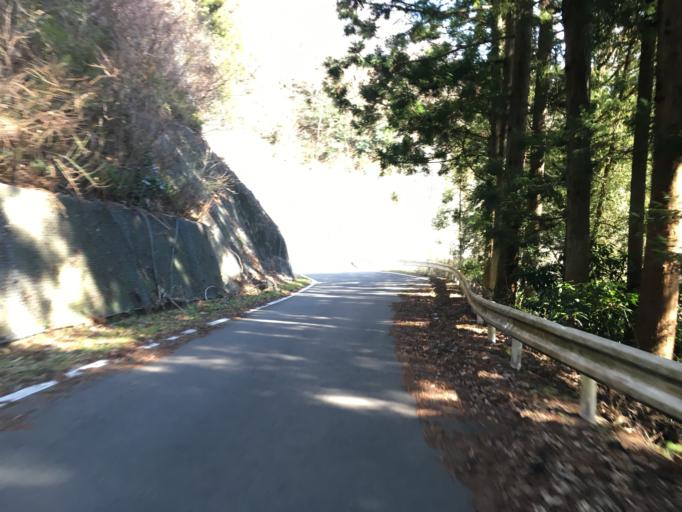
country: JP
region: Ibaraki
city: Kitaibaraki
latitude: 36.7842
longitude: 140.6755
